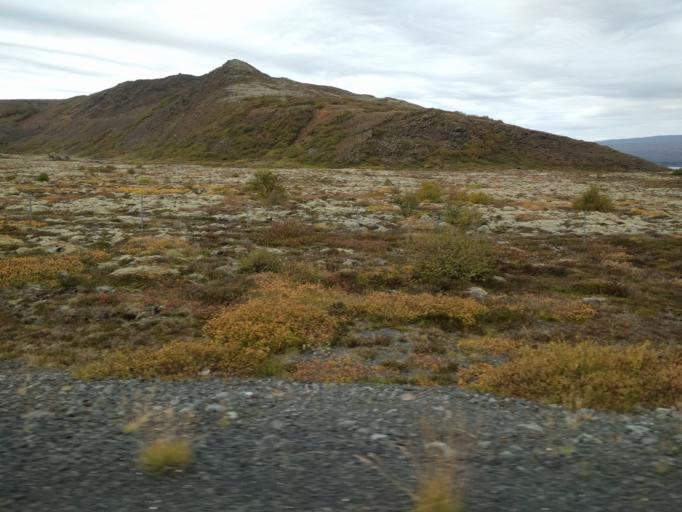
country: IS
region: South
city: Hveragerdi
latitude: 64.2246
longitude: -21.0535
